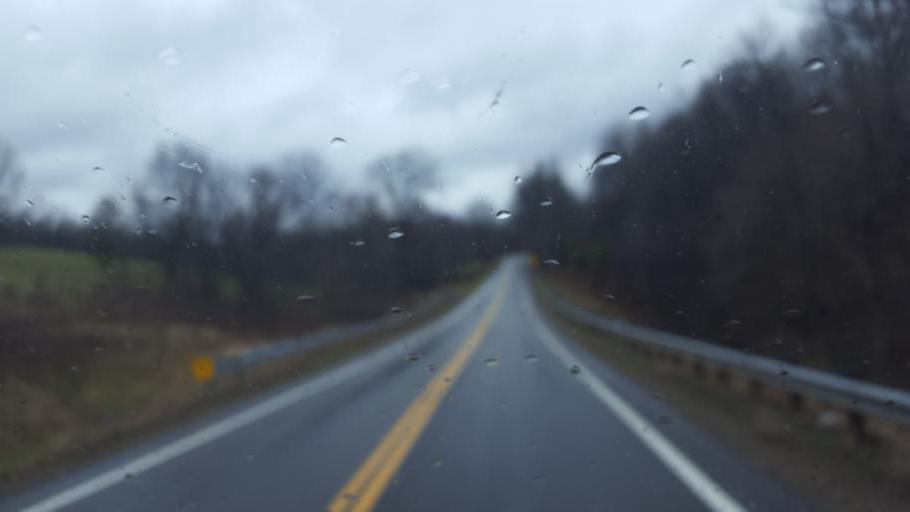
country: US
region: Ohio
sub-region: Sandusky County
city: Bellville
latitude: 40.6133
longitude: -82.4067
